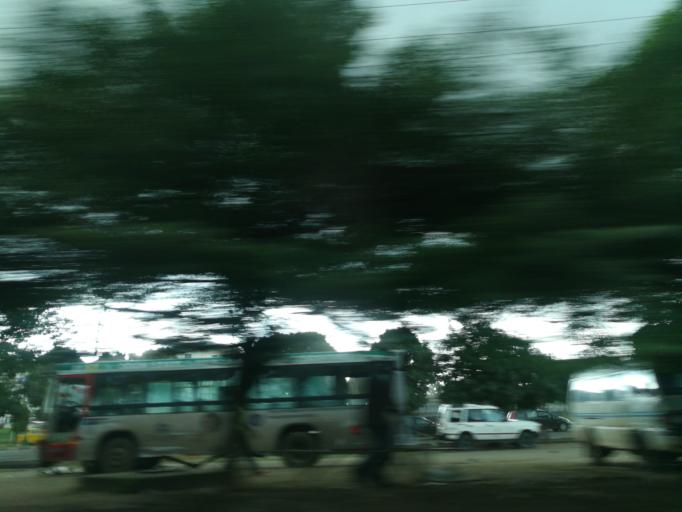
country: NG
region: Lagos
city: Ojota
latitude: 6.6012
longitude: 3.3776
